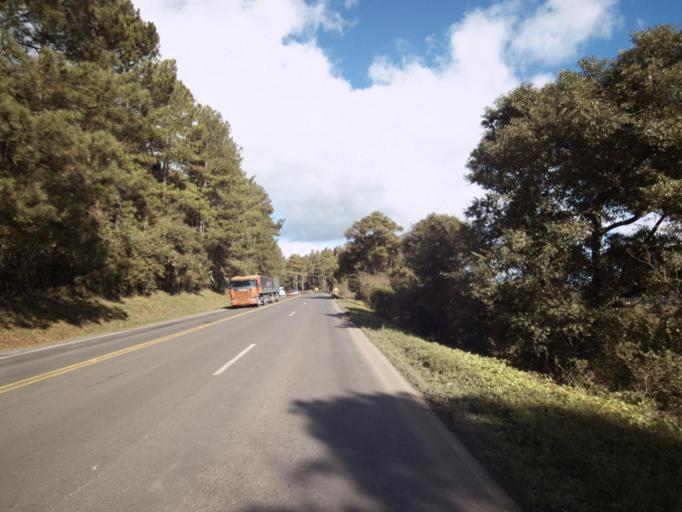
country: BR
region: Santa Catarina
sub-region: Joacaba
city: Joacaba
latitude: -27.0141
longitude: -51.7366
